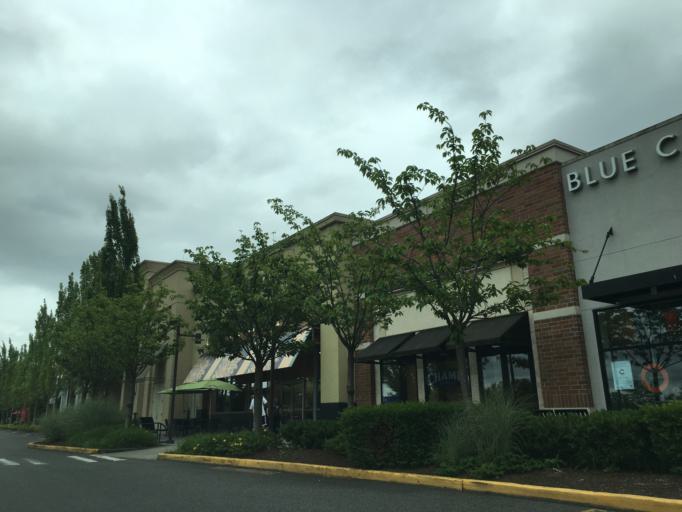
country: US
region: Washington
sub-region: Snohomish County
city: Alderwood Manor
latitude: 47.8310
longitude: -122.2732
